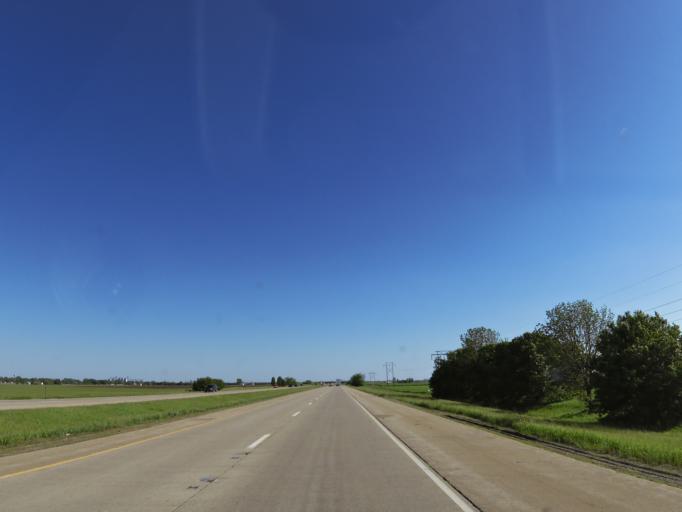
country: US
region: Illinois
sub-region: Marshall County
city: Wenona
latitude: 41.1589
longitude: -89.0758
